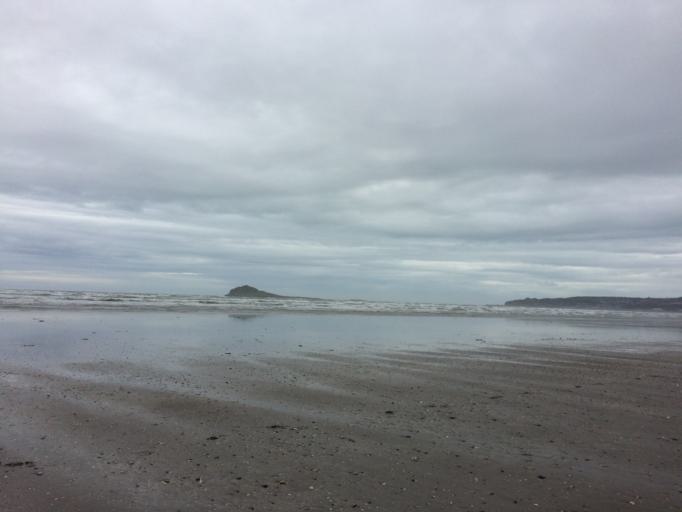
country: IE
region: Leinster
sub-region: Fingal County
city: Baldoyle
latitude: 53.4113
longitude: -6.1160
